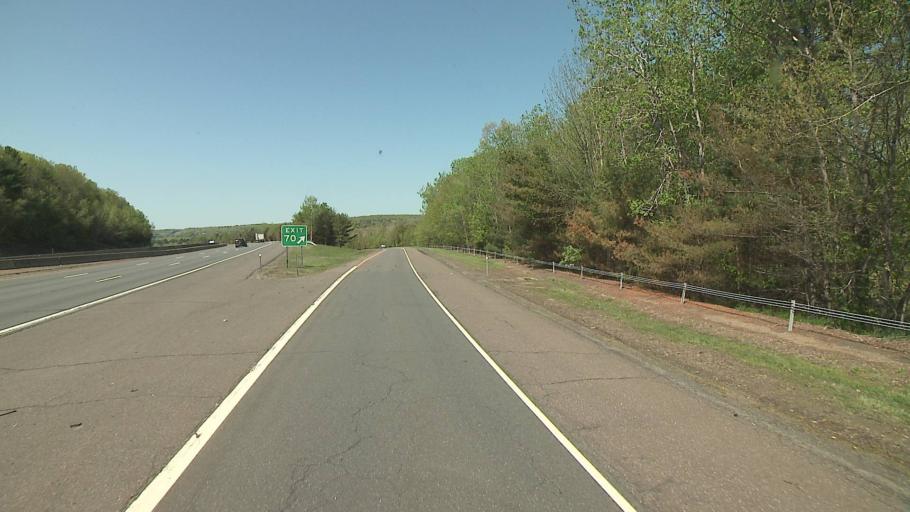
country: US
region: Connecticut
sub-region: Tolland County
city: Stafford Springs
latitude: 41.9032
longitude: -72.2816
